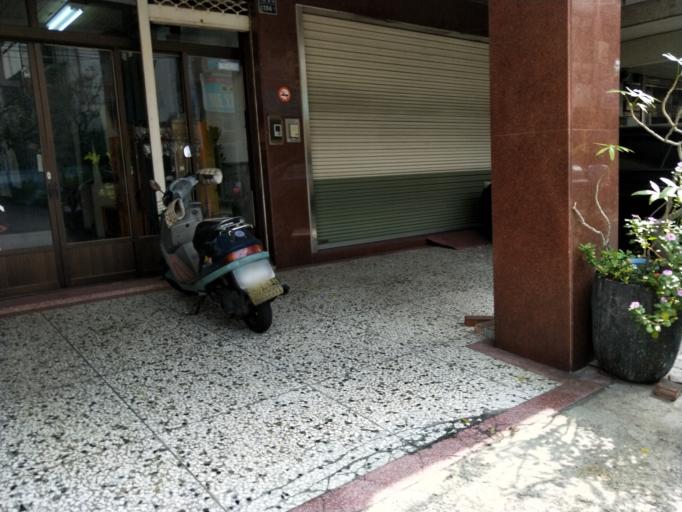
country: TW
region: Taiwan
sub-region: Changhua
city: Chang-hua
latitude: 24.0854
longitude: 120.5443
